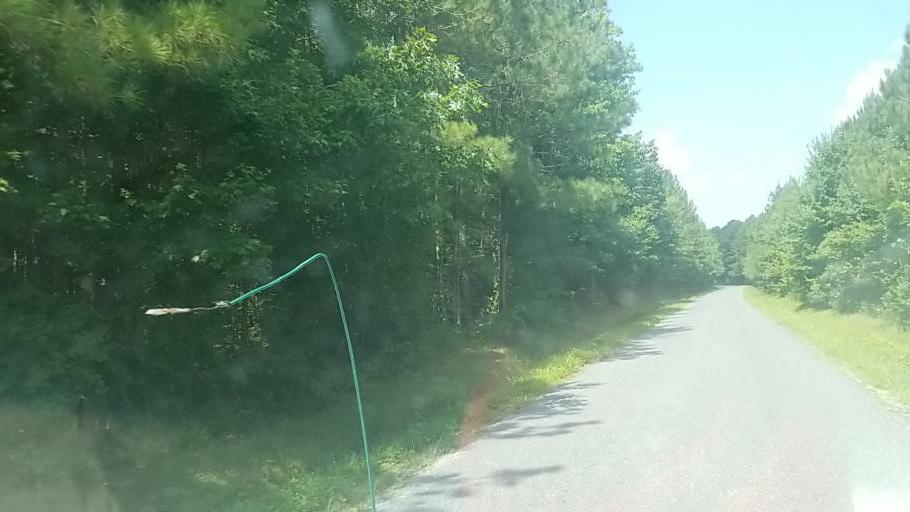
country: US
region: Maryland
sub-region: Worcester County
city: Berlin
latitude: 38.2863
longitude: -75.3070
